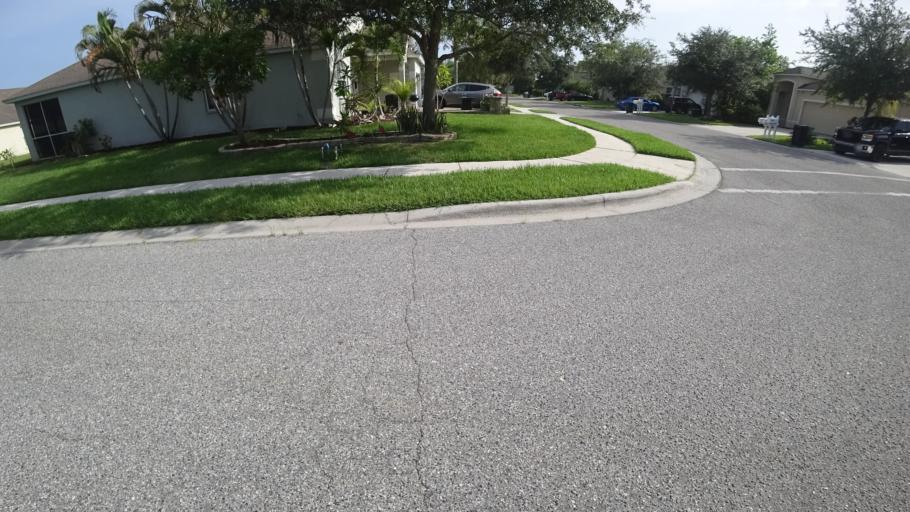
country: US
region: Florida
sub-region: Manatee County
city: Ellenton
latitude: 27.5528
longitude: -82.4966
